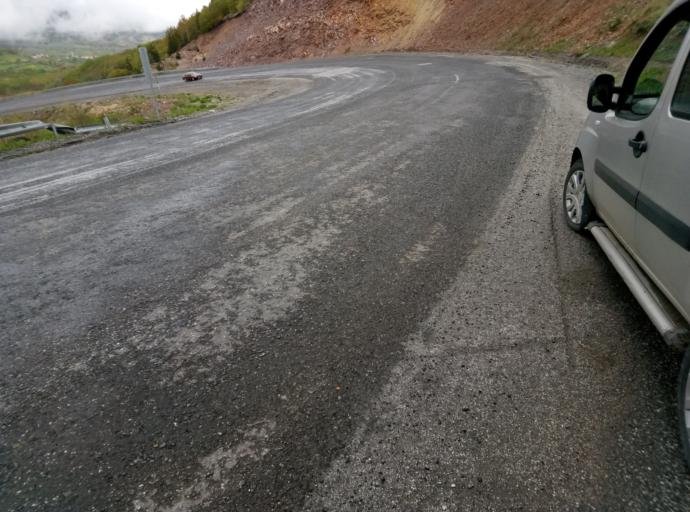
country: TR
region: Sivas
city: Aksu
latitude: 39.9954
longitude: 37.9792
